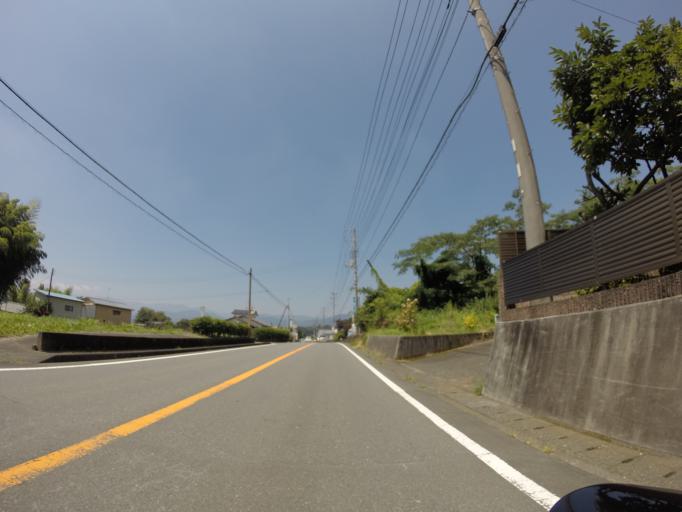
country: JP
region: Shizuoka
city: Fujinomiya
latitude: 35.2699
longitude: 138.6224
